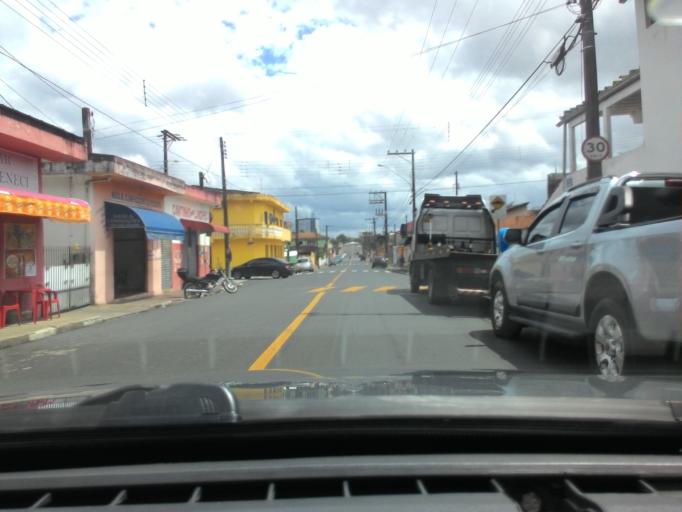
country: BR
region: Sao Paulo
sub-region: Registro
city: Registro
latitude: -24.5038
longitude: -47.8433
